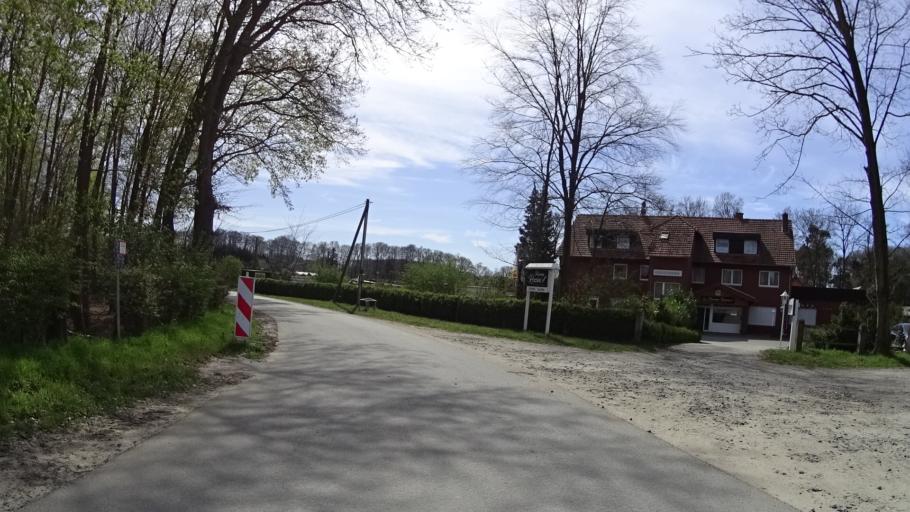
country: DE
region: Lower Saxony
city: Emsburen
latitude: 52.4561
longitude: 7.3289
